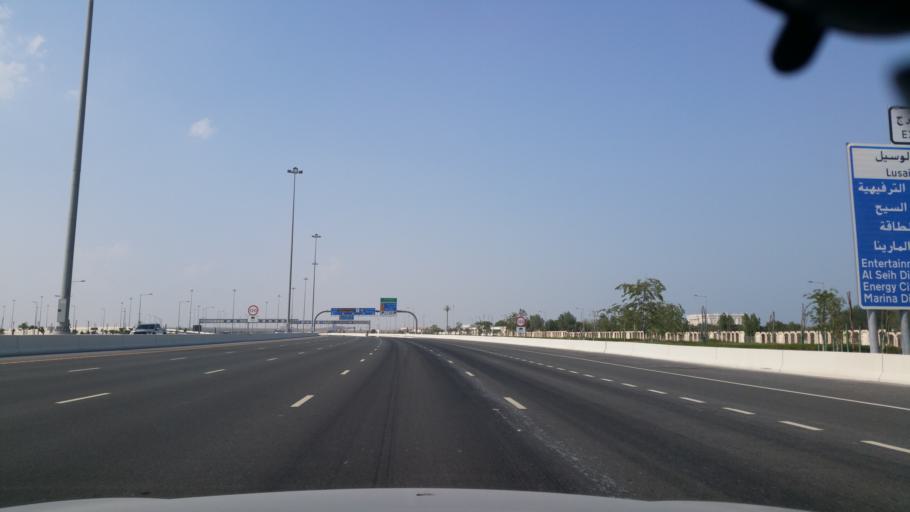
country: QA
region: Baladiyat Umm Salal
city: Umm Salal Muhammad
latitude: 25.3849
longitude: 51.5003
